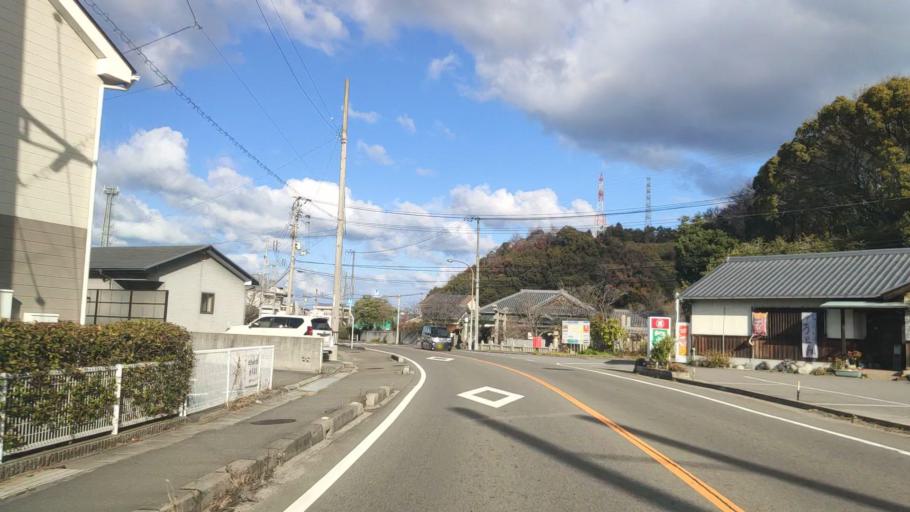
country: JP
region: Ehime
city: Masaki-cho
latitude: 33.8404
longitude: 132.7091
